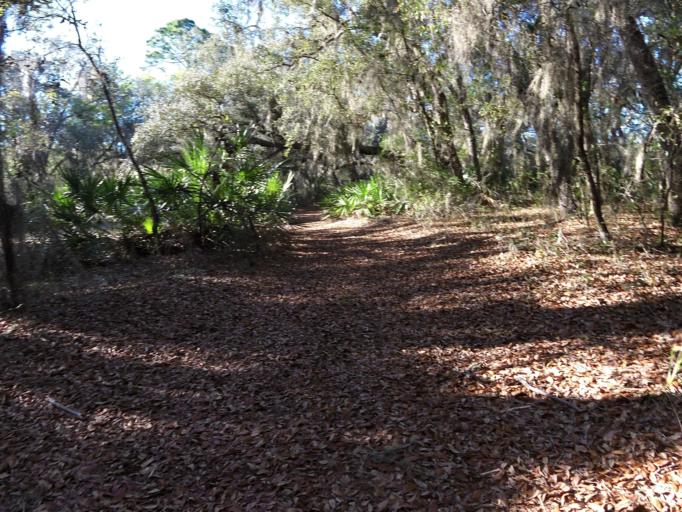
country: US
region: Florida
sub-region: Clay County
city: Keystone Heights
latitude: 29.8207
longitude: -82.0219
